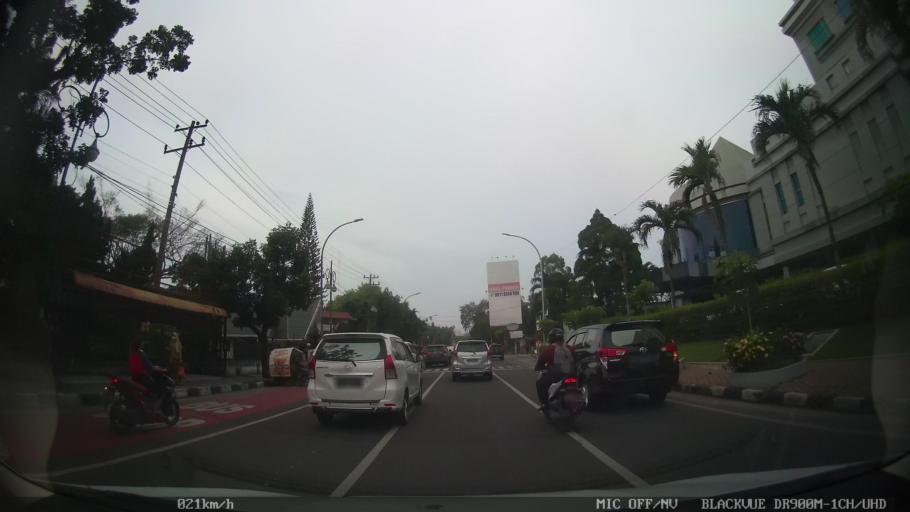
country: ID
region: North Sumatra
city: Medan
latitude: 3.5983
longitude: 98.6818
